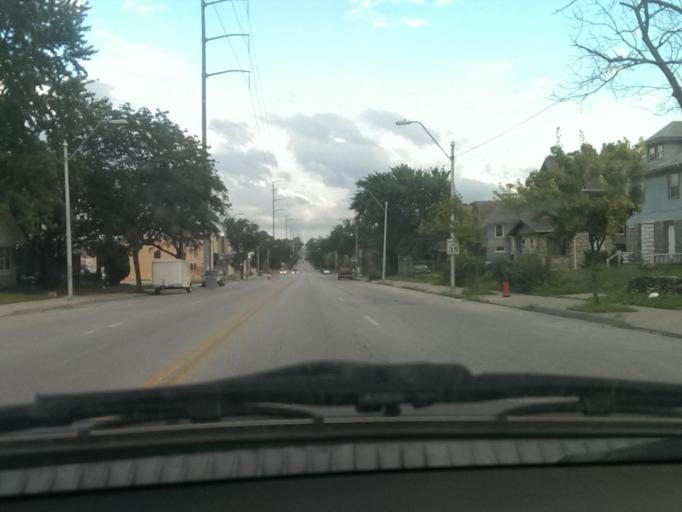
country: US
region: Kansas
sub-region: Johnson County
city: Westwood
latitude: 39.0466
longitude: -94.5727
